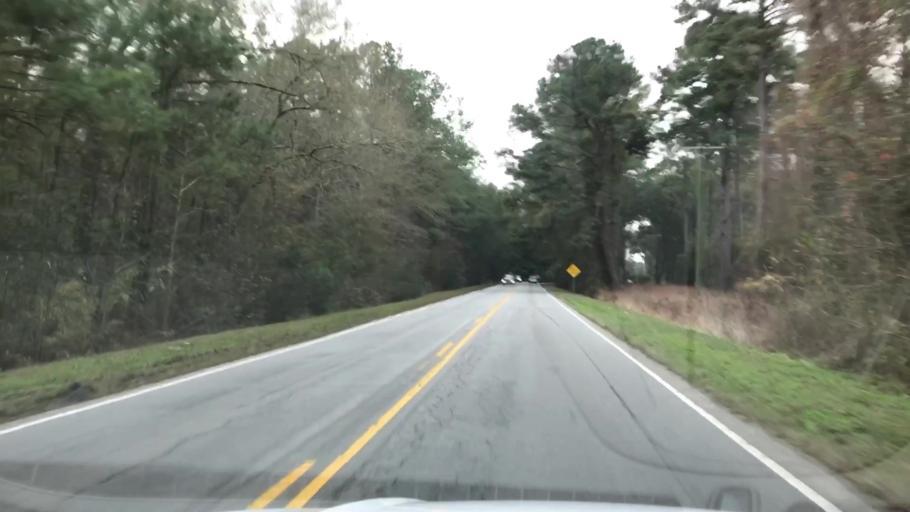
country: US
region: South Carolina
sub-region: Jasper County
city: Ridgeland
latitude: 32.3901
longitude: -80.9076
